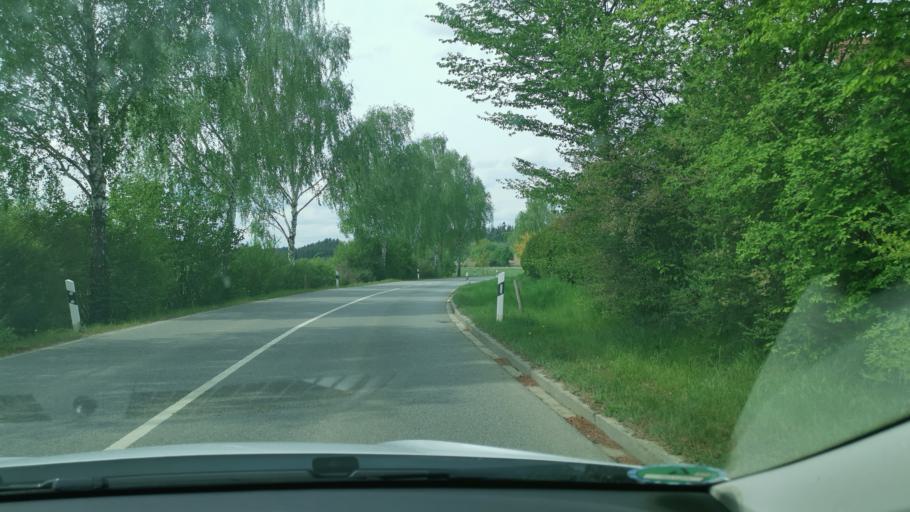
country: DE
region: Bavaria
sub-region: Upper Bavaria
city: Petershausen
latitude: 48.4109
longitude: 11.4638
